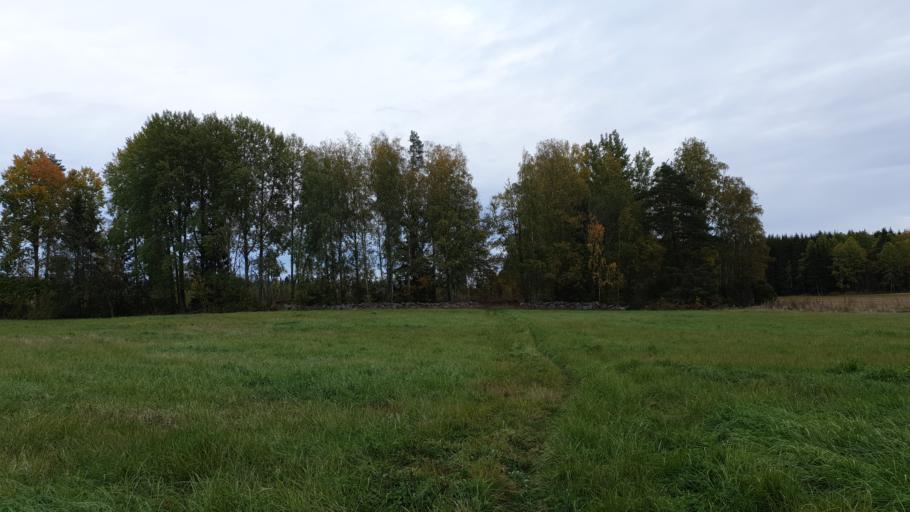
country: SE
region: Vaestmanland
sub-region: Sala Kommun
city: Sala
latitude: 59.8147
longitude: 16.6527
